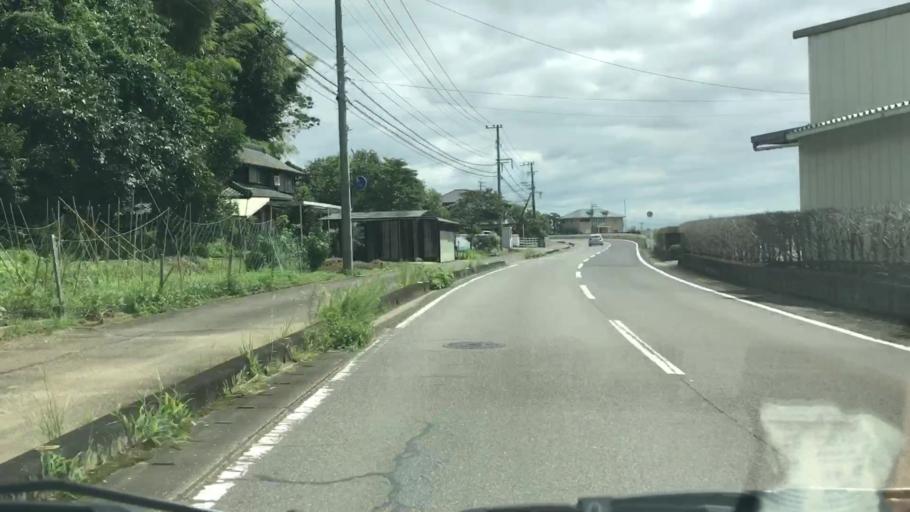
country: JP
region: Saga Prefecture
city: Kashima
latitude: 33.2288
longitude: 130.1531
